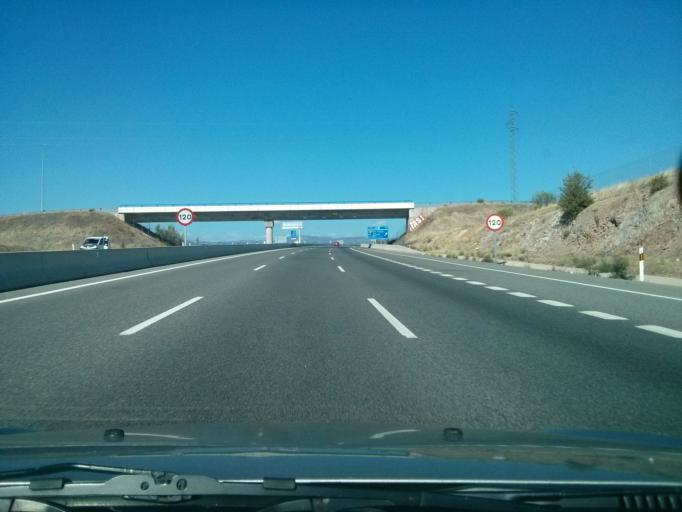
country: ES
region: Madrid
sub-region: Provincia de Madrid
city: Pedrezuela
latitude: 40.7527
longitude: -3.5925
